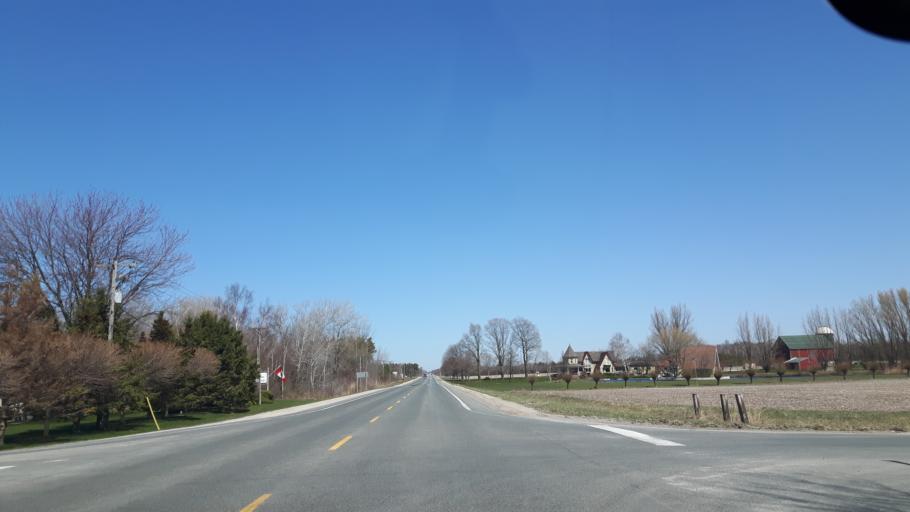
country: CA
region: Ontario
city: Goderich
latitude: 43.6982
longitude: -81.7056
